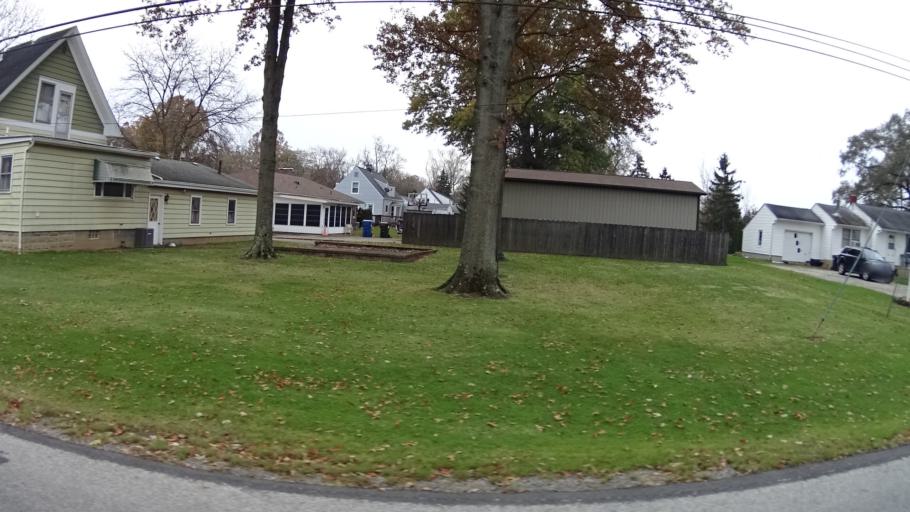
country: US
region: Ohio
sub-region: Lorain County
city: Elyria
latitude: 41.3380
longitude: -82.0908
